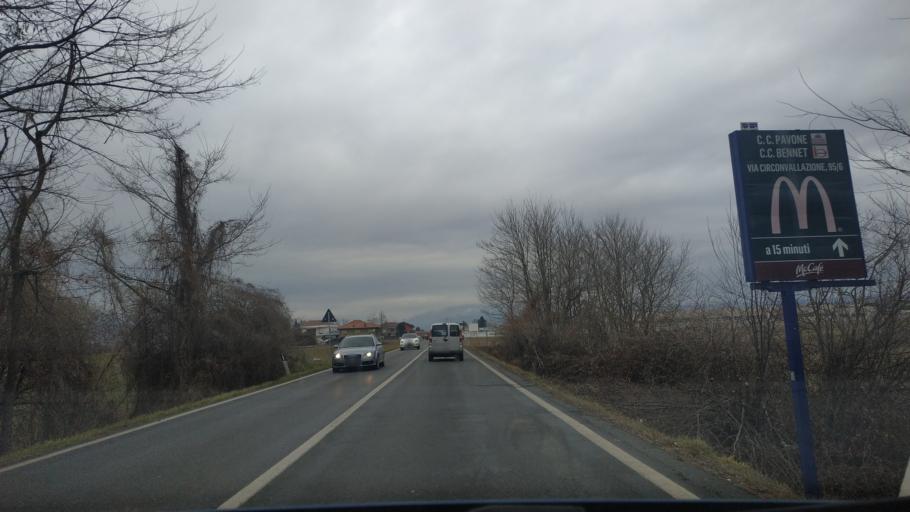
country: IT
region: Piedmont
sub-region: Provincia di Torino
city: Strambino
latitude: 45.3909
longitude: 7.8848
